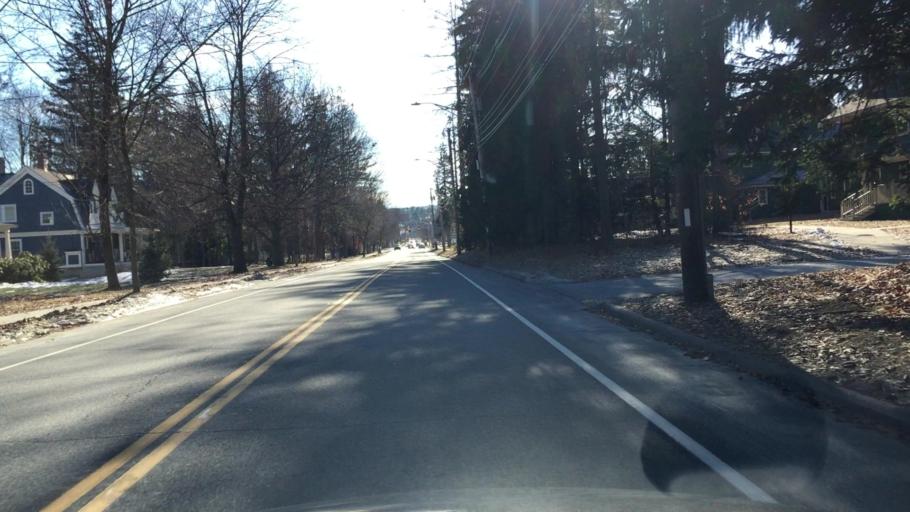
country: US
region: New Hampshire
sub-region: Grafton County
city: Hanover
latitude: 43.7063
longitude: -72.2829
